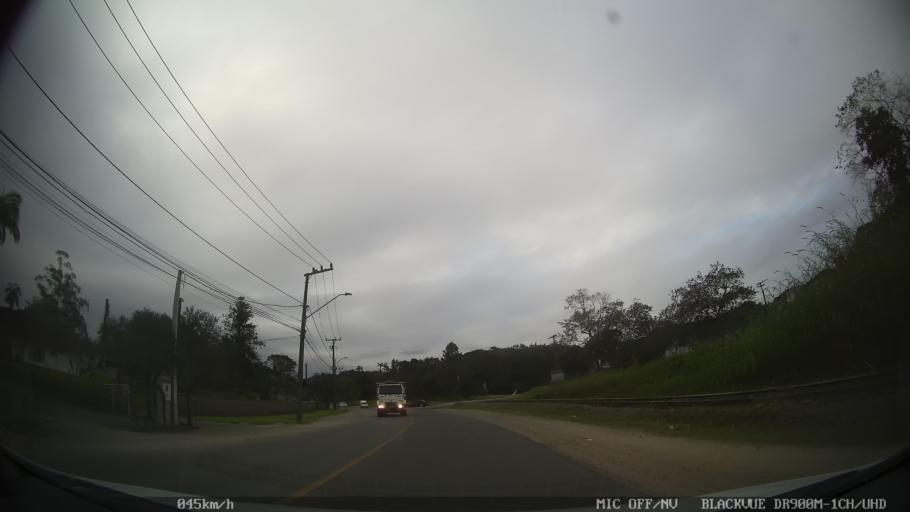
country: BR
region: Santa Catarina
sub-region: Joinville
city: Joinville
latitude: -26.3376
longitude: -48.8786
